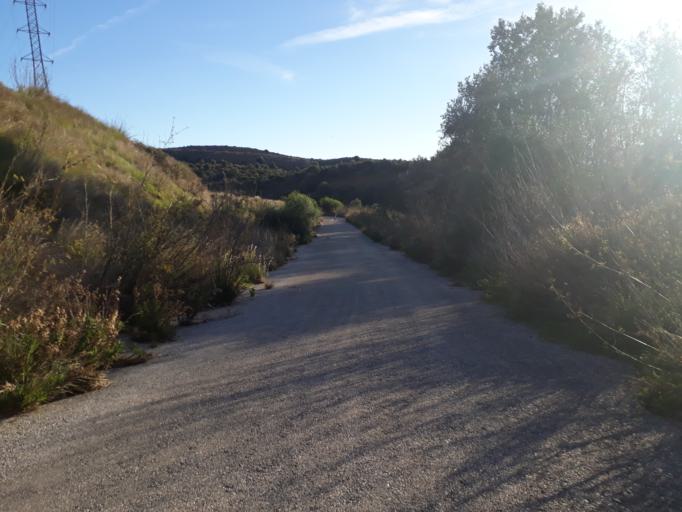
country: ES
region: Andalusia
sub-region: Provincia de Malaga
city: Fuengirola
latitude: 36.5033
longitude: -4.7006
